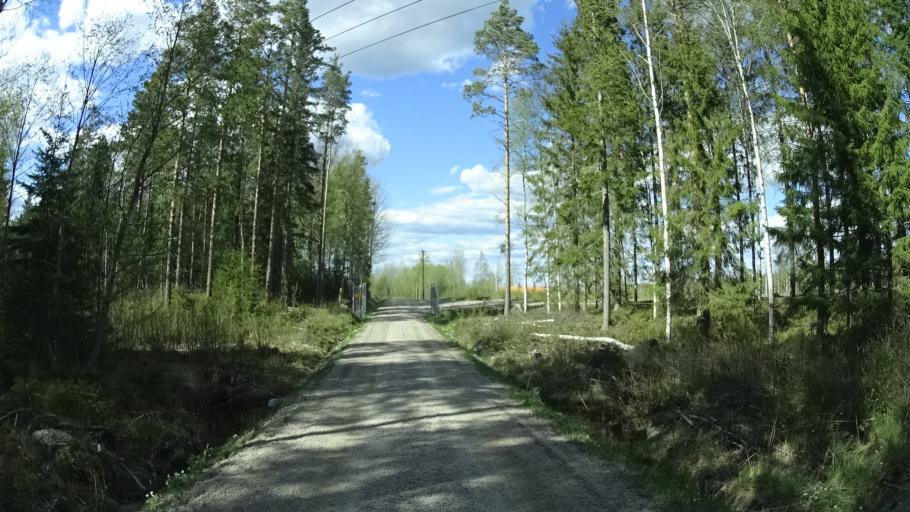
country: SE
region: OErebro
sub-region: Orebro Kommun
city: Garphyttan
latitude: 59.4231
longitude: 14.8656
